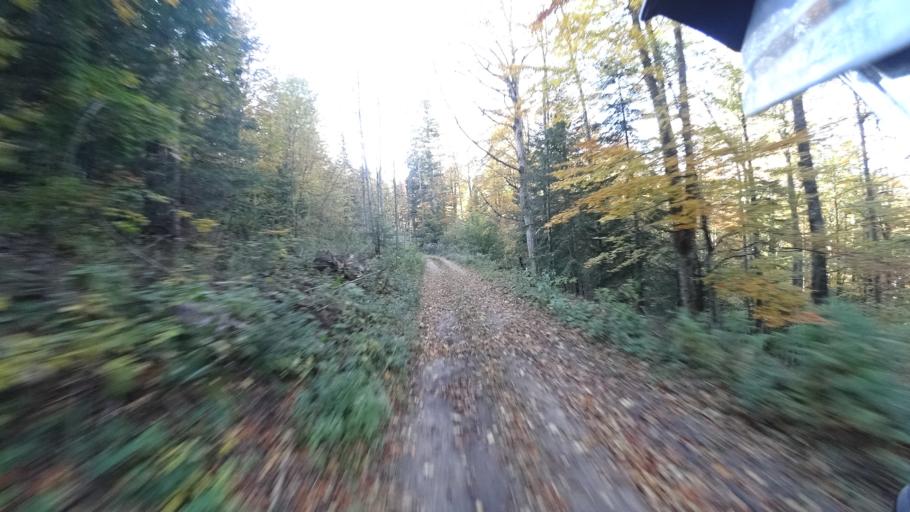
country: HR
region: Karlovacka
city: Plaski
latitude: 45.0178
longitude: 15.3794
